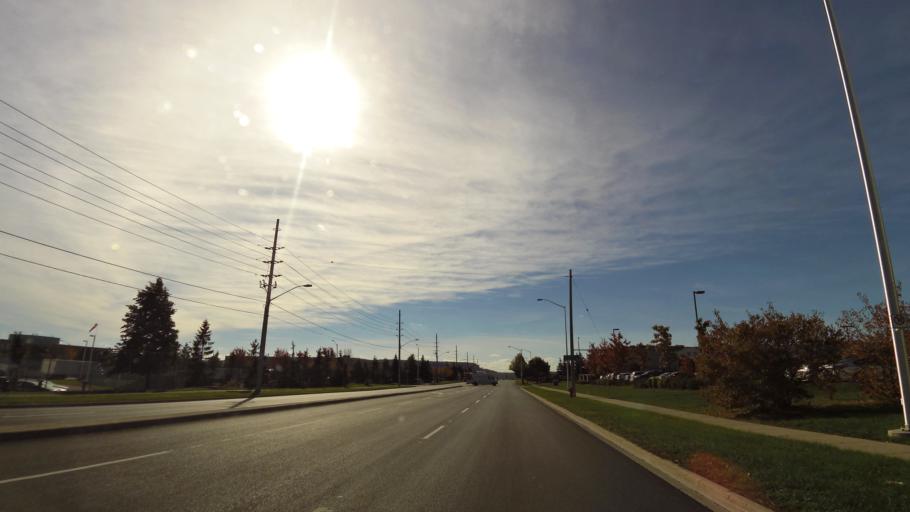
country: CA
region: Ontario
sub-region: Halton
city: Milton
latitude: 43.5368
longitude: -79.9105
